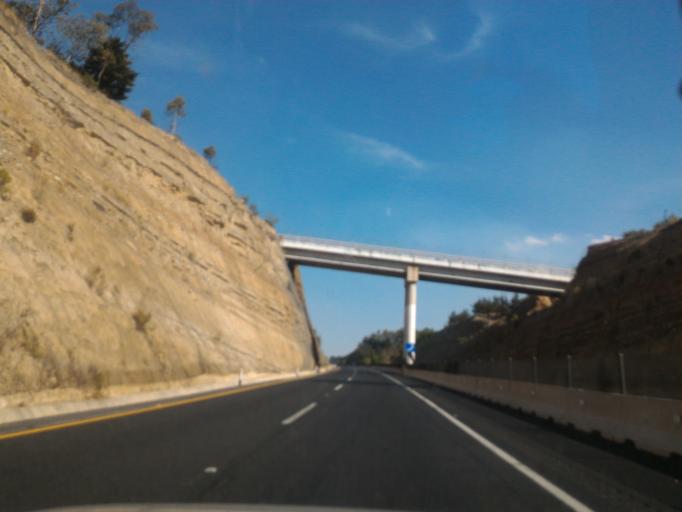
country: MX
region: Mexico
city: Temascalcingo de Jose Maria Velazco
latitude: 19.8534
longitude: -100.0263
